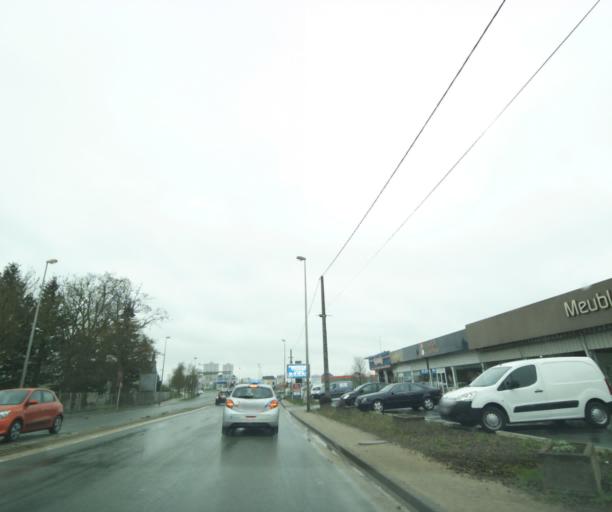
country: FR
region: Centre
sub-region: Departement du Loiret
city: Saran
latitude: 47.9400
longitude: 1.8934
